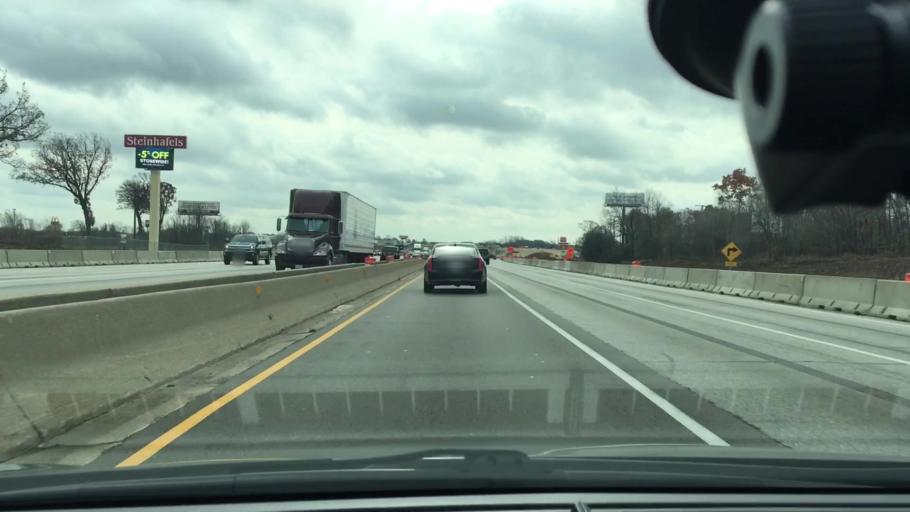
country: US
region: Wisconsin
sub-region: Racine County
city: Caledonia
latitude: 42.8787
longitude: -87.9371
